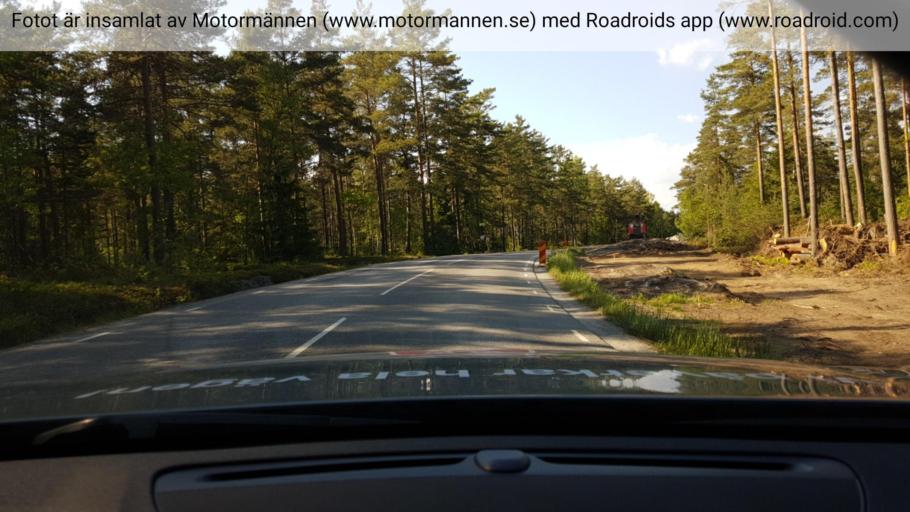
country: SE
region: Stockholm
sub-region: Varmdo Kommun
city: Mortnas
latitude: 59.2698
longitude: 18.4268
